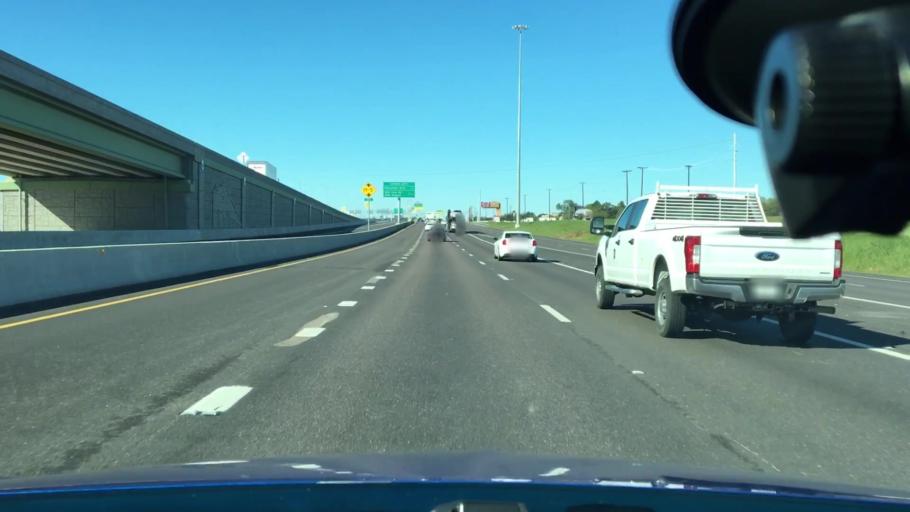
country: US
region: Texas
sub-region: Dallas County
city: Irving
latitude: 32.8373
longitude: -96.9204
